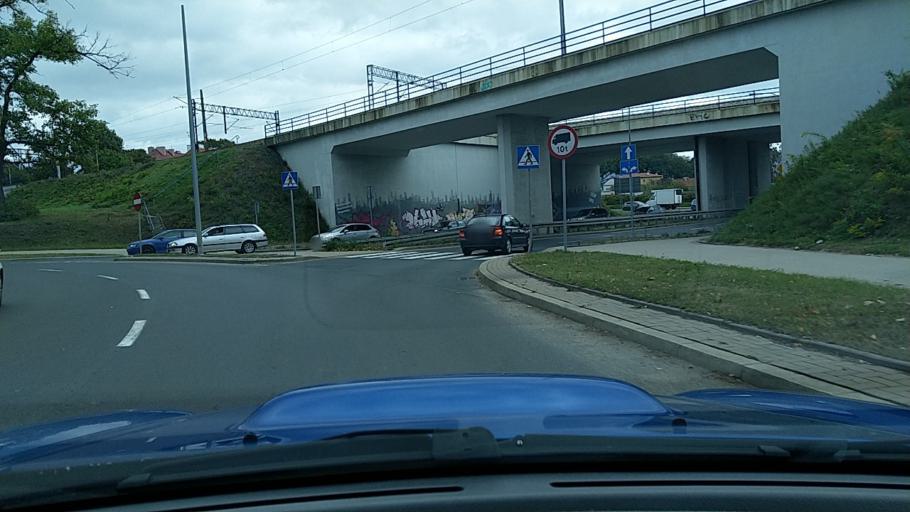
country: PL
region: Warmian-Masurian Voivodeship
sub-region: Olsztyn
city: Kortowo
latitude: 53.7776
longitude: 20.4636
